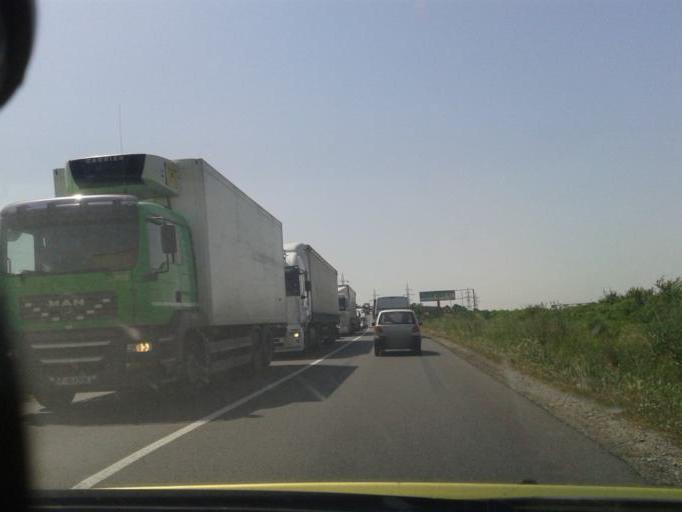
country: RO
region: Ilfov
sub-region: Comuna Glina
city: Catelu
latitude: 44.4269
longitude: 26.2352
